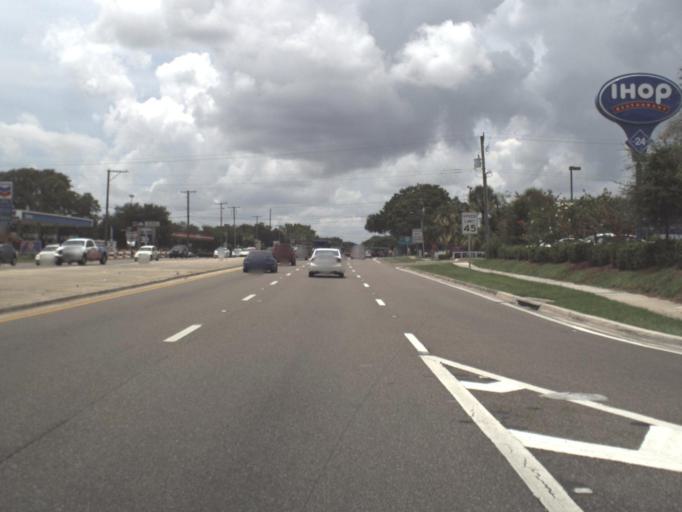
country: US
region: Florida
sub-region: Hillsborough County
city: Lake Magdalene
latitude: 28.0881
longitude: -82.4555
